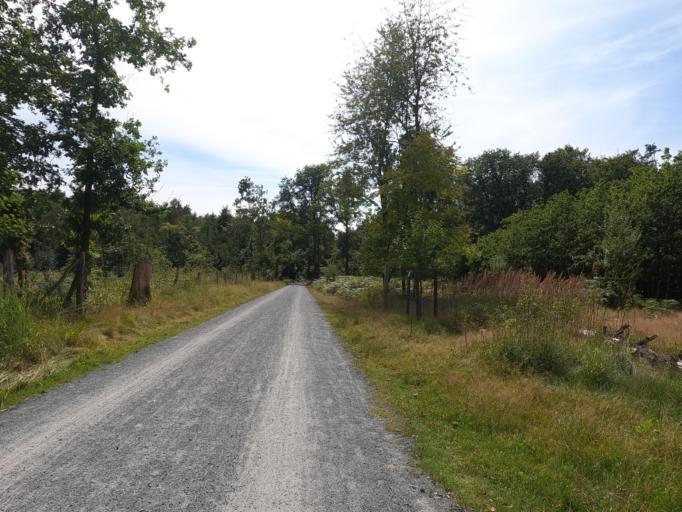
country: DE
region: Hesse
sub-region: Regierungsbezirk Darmstadt
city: Neu Isenburg
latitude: 50.0699
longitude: 8.7134
